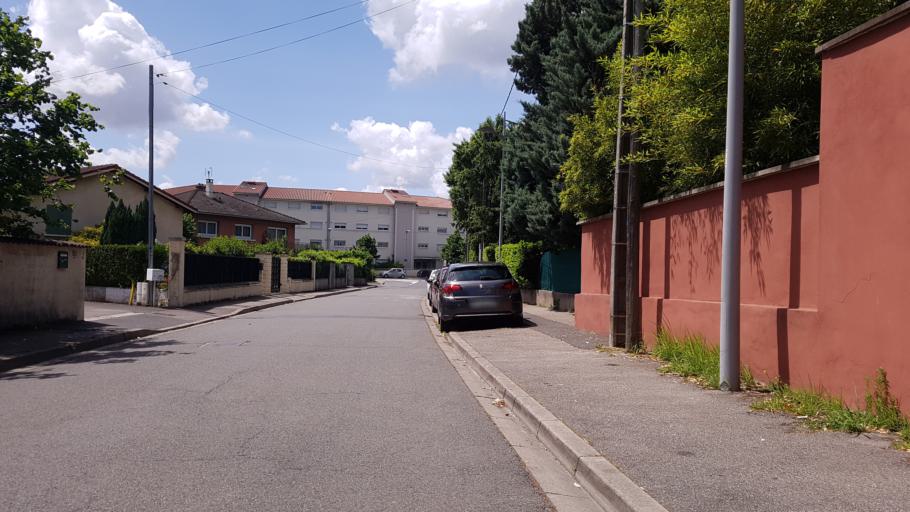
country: FR
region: Rhone-Alpes
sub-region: Departement du Rhone
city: Rillieux-la-Pape
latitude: 45.8198
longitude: 4.8868
